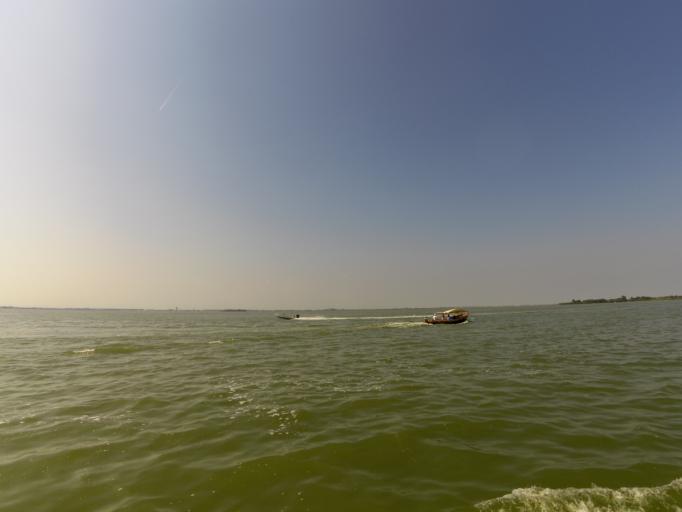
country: IT
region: Veneto
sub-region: Provincia di Venezia
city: Burano
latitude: 45.4768
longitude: 12.3911
